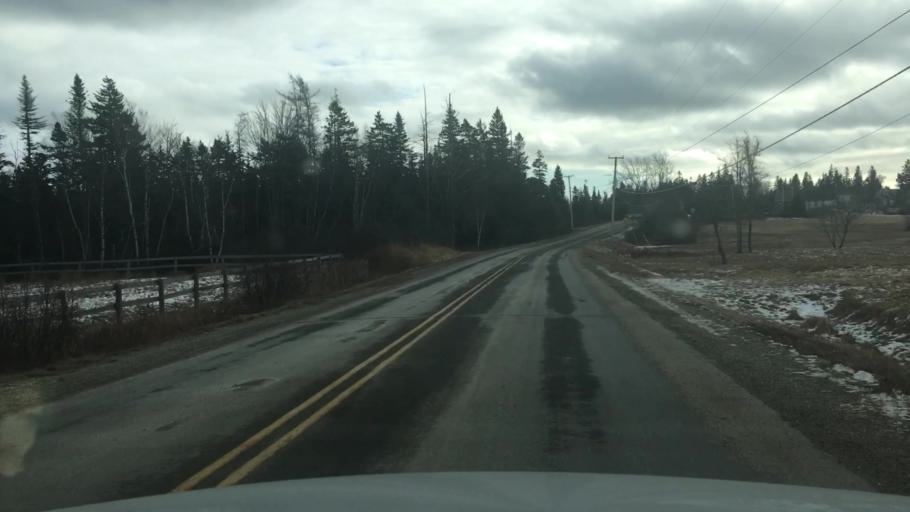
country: US
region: Maine
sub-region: Washington County
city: Machias
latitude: 44.6169
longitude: -67.4795
